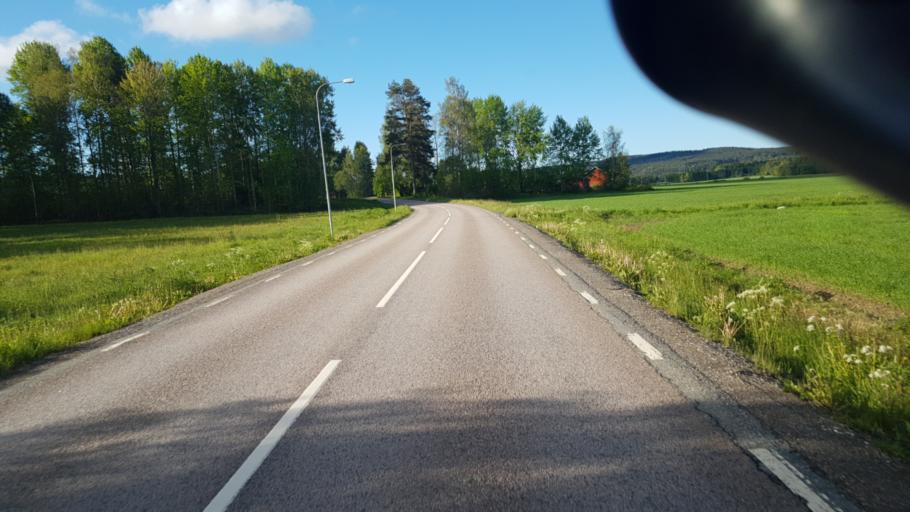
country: SE
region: Vaermland
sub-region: Arvika Kommun
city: Arvika
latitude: 59.5751
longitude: 12.5540
